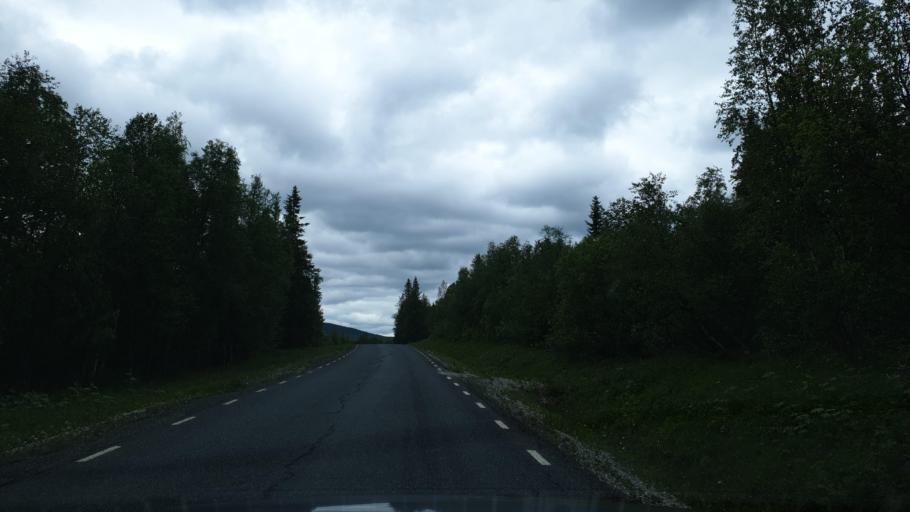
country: SE
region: Vaesterbotten
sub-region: Vilhelmina Kommun
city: Sjoberg
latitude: 65.2818
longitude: 15.3008
